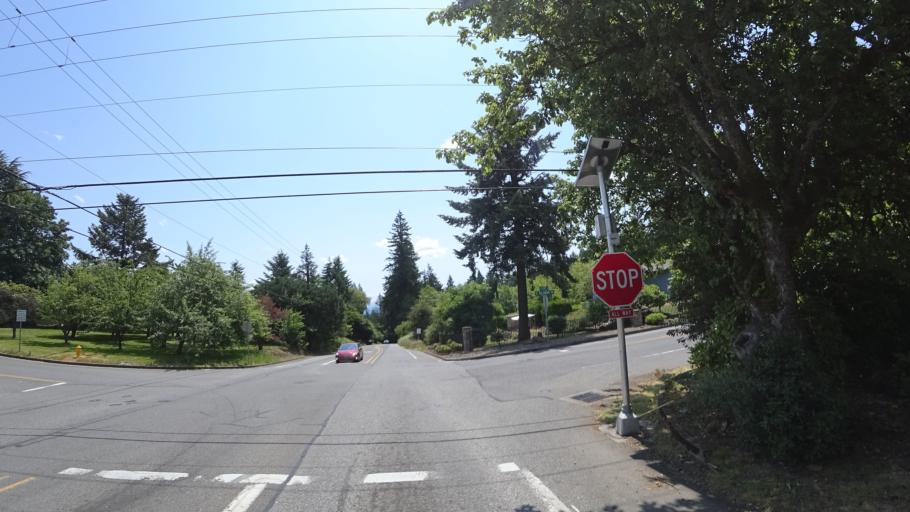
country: US
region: Oregon
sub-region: Clackamas County
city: Happy Valley
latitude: 45.4537
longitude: -122.5394
